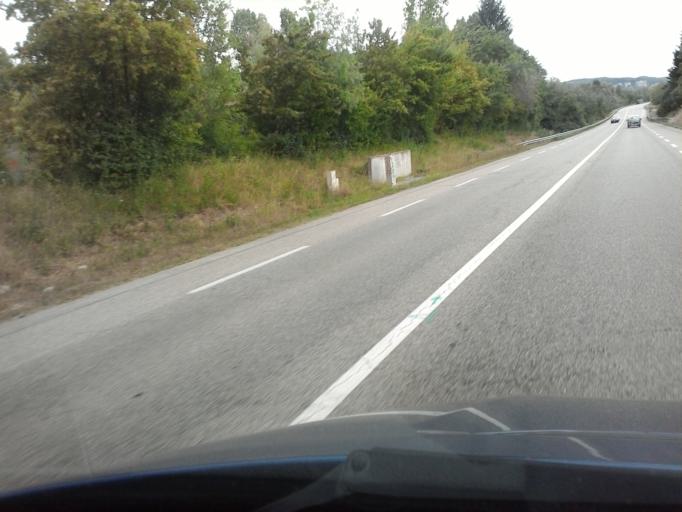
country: FR
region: Rhone-Alpes
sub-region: Departement de l'Ain
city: Lagnieu
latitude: 45.9001
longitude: 5.3373
